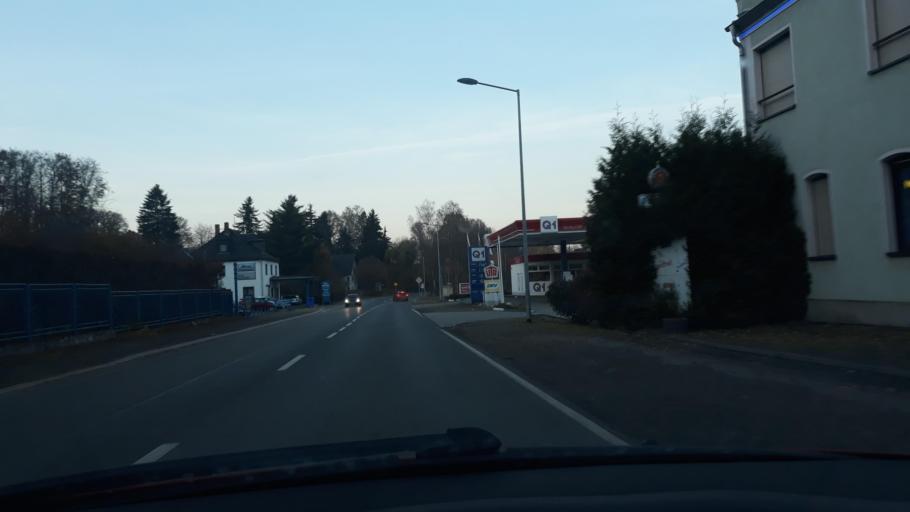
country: DE
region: Saxony
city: Kirchberg
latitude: 50.6291
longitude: 12.5197
